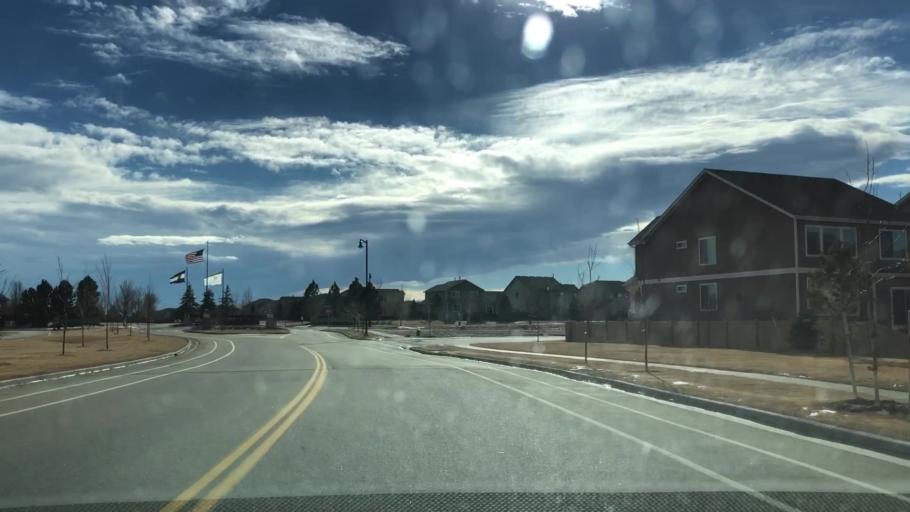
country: US
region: Colorado
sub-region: Weld County
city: Windsor
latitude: 40.5097
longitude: -104.9546
